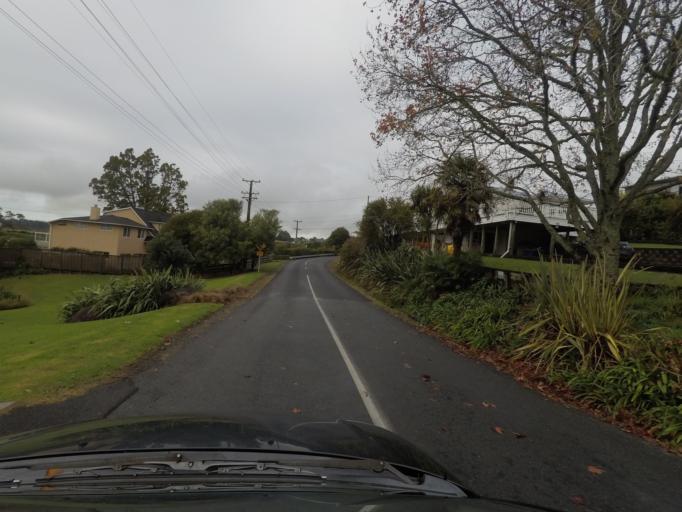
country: NZ
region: Auckland
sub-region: Auckland
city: Rosebank
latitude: -36.7617
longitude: 174.5975
